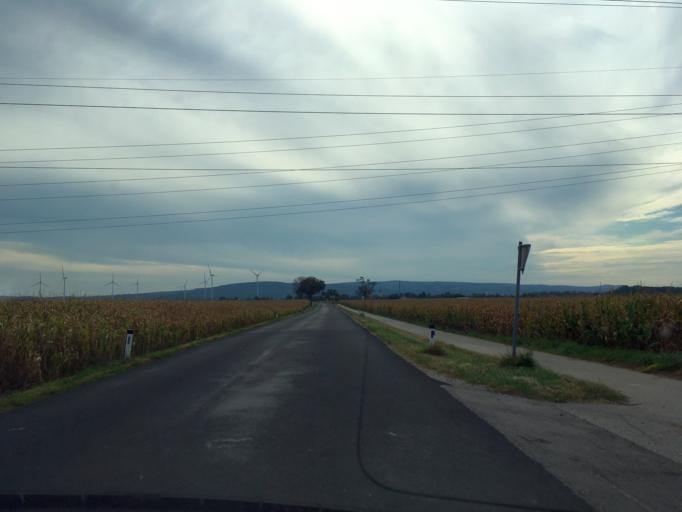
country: AT
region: Lower Austria
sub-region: Politischer Bezirk Bruck an der Leitha
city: Trautmannsdorf an der Leitha
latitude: 48.0305
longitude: 16.6781
